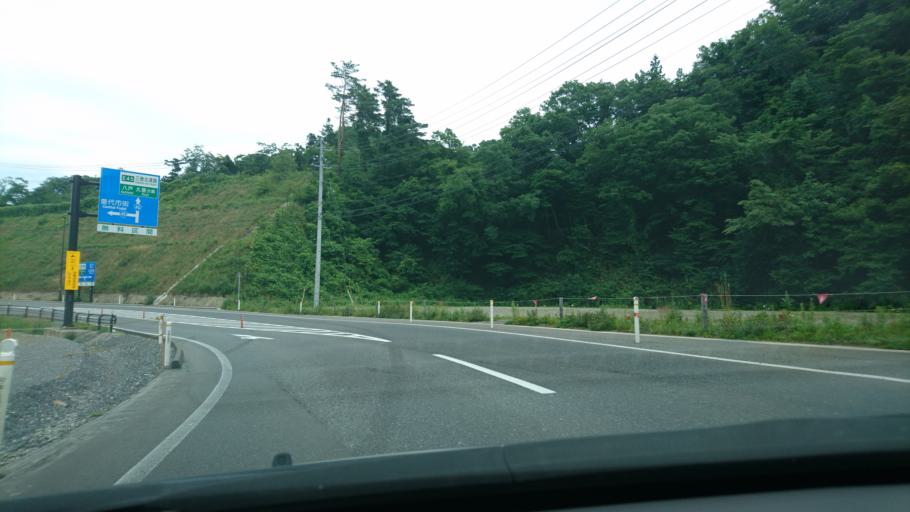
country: JP
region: Iwate
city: Miyako
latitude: 39.9915
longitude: 141.8786
